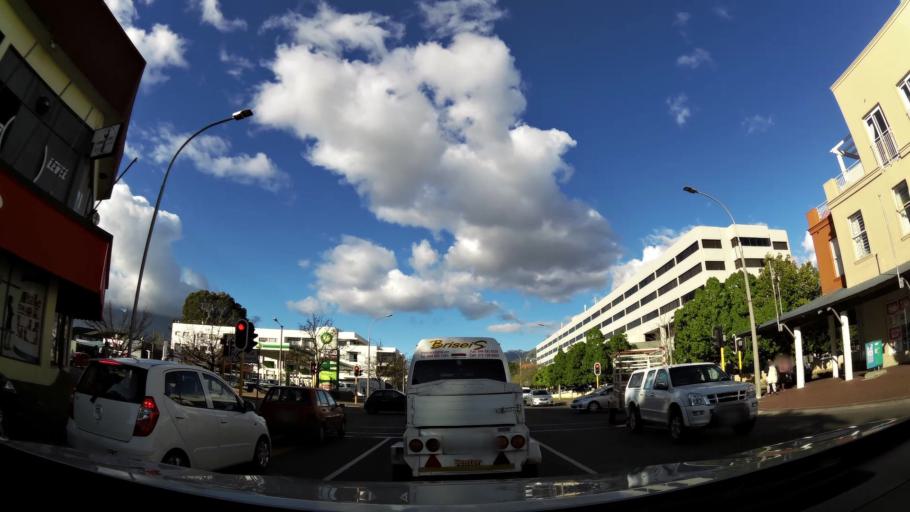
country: ZA
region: Western Cape
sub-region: Cape Winelands District Municipality
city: Stellenbosch
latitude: -33.9321
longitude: 18.8599
